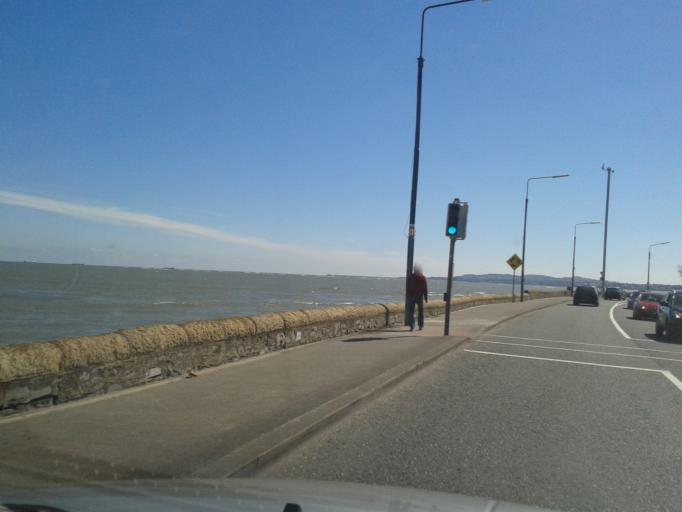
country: IE
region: Leinster
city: Sandymount
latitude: 53.3334
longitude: -6.2116
